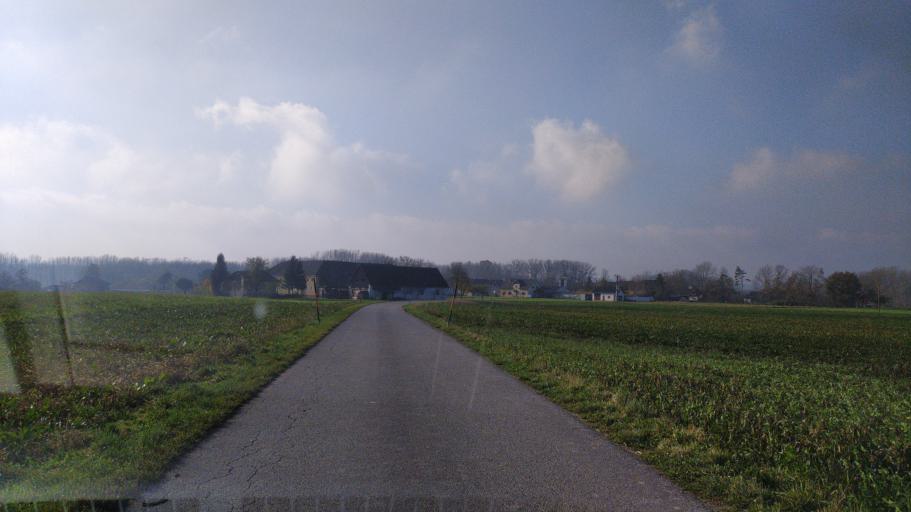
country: AT
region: Lower Austria
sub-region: Politischer Bezirk Amstetten
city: Strengberg
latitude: 48.1857
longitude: 14.6519
